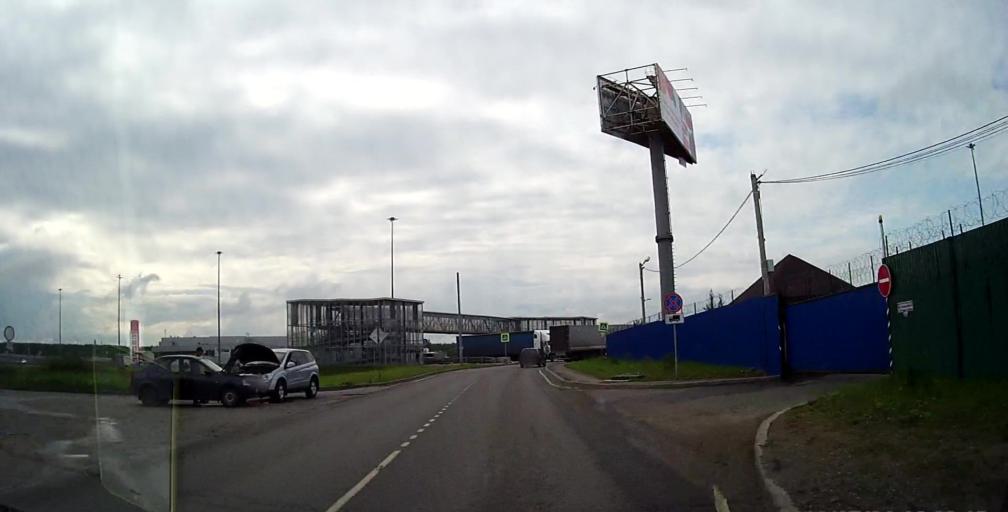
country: RU
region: Moskovskaya
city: Klimovsk
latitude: 55.3888
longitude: 37.5534
